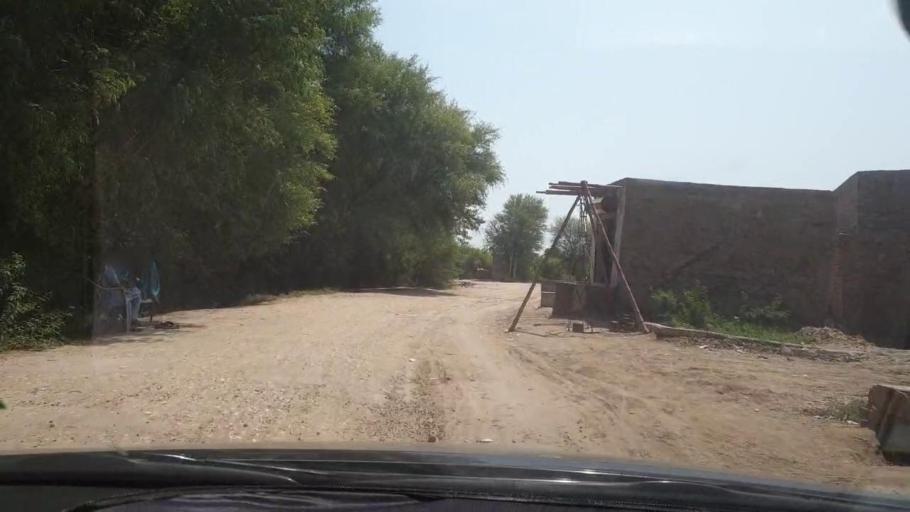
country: PK
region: Sindh
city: Naukot
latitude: 24.7687
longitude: 69.1951
